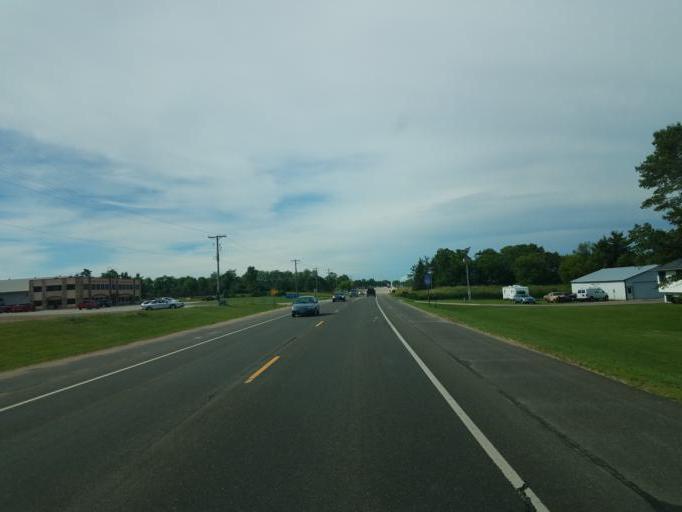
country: US
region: Wisconsin
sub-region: Monroe County
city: Tomah
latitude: 43.9524
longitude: -90.5046
